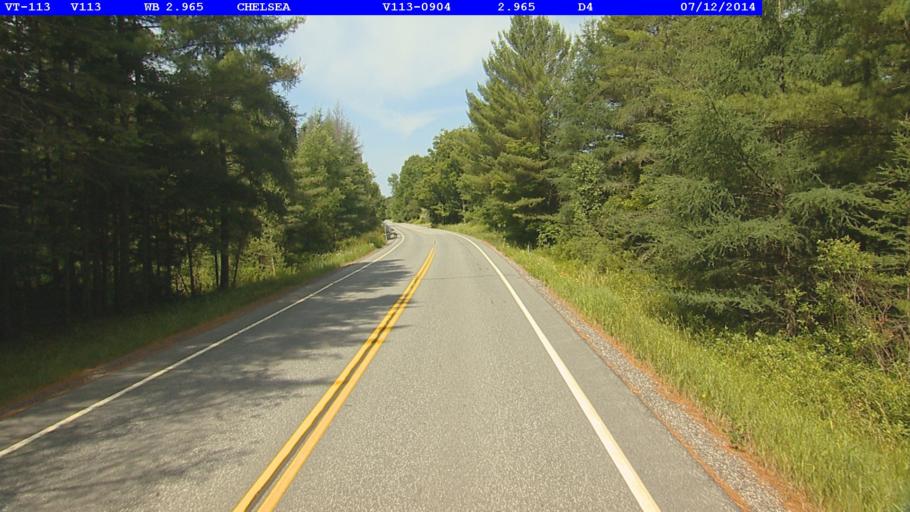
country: US
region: Vermont
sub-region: Orange County
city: Chelsea
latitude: 43.9922
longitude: -72.3937
